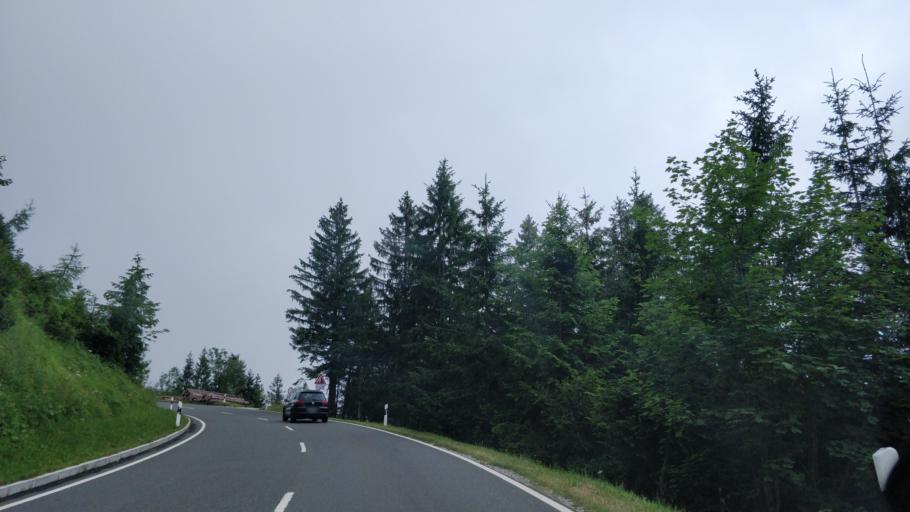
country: AT
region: Salzburg
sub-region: Politischer Bezirk Hallein
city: Hallein
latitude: 47.6351
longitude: 13.0866
